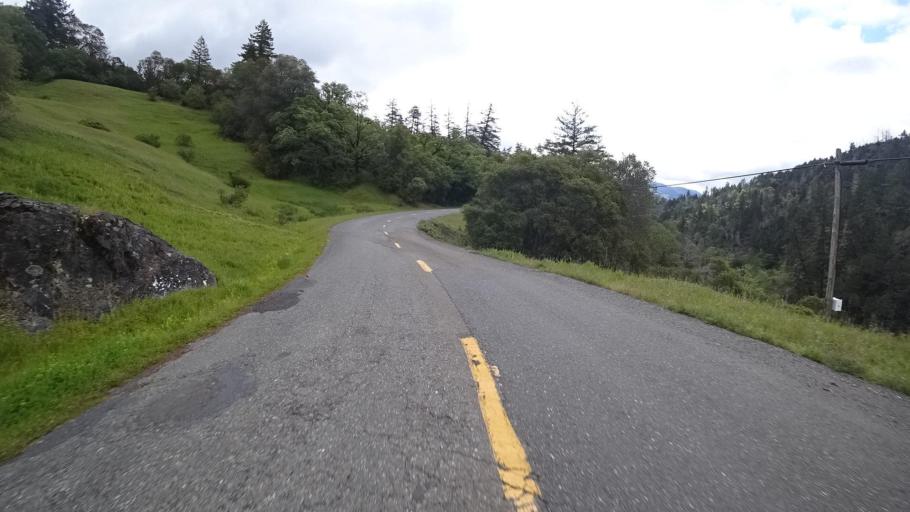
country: US
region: California
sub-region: Humboldt County
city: Redway
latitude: 40.2254
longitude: -123.6067
